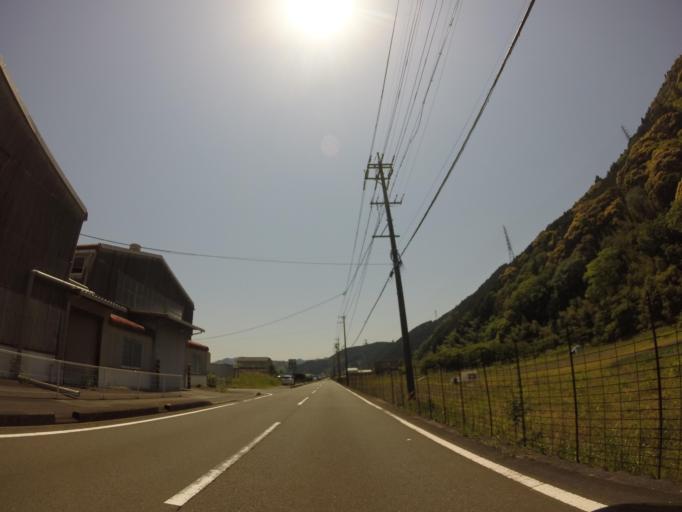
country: JP
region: Shizuoka
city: Shizuoka-shi
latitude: 35.0009
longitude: 138.2831
